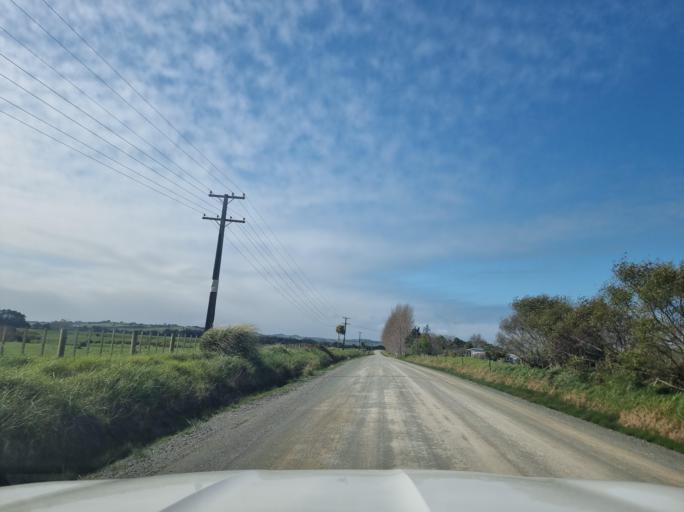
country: NZ
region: Auckland
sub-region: Auckland
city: Wellsford
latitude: -36.1155
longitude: 174.5004
